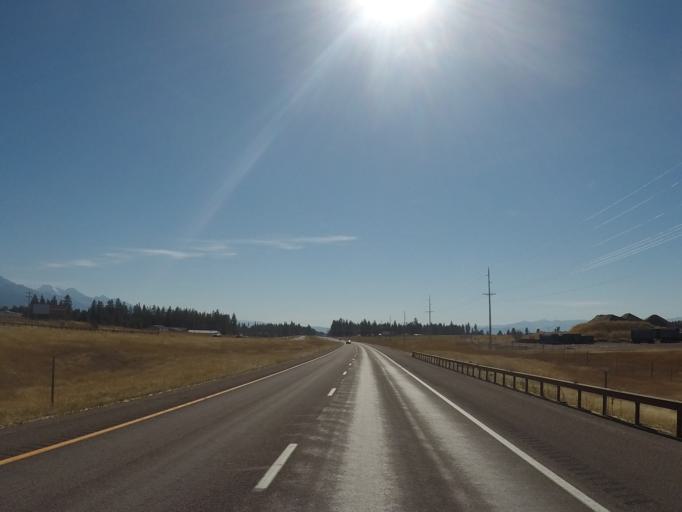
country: US
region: Montana
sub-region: Lake County
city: Pablo
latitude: 47.6372
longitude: -114.1143
